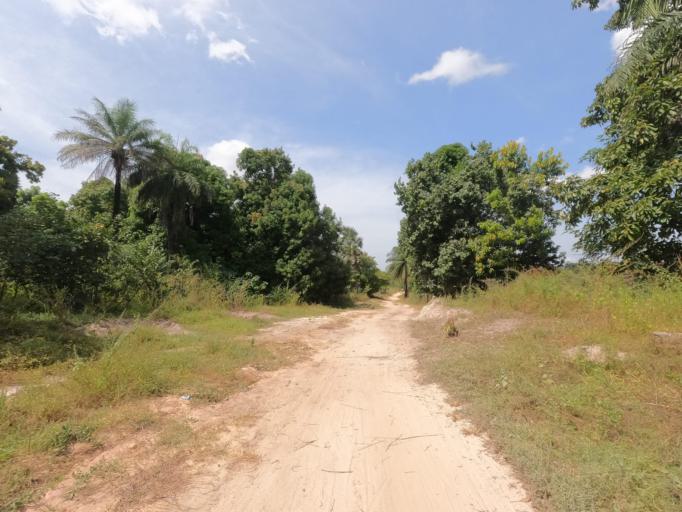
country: SN
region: Sedhiou
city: Sedhiou
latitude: 12.4605
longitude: -15.5872
